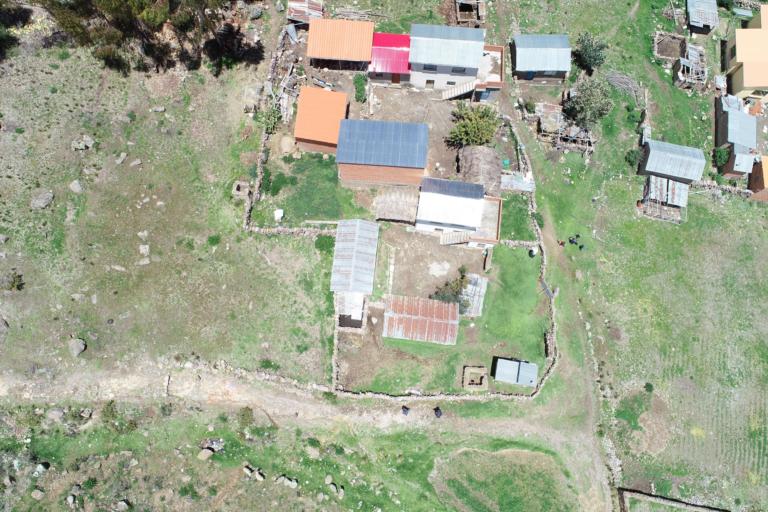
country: BO
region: La Paz
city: Achacachi
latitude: -16.0243
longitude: -68.7921
